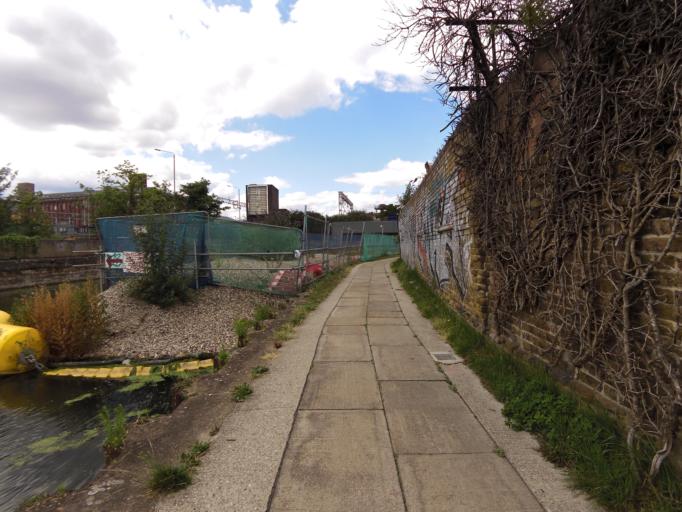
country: GB
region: England
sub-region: Greater London
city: Poplar
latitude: 51.5314
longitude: -0.0172
